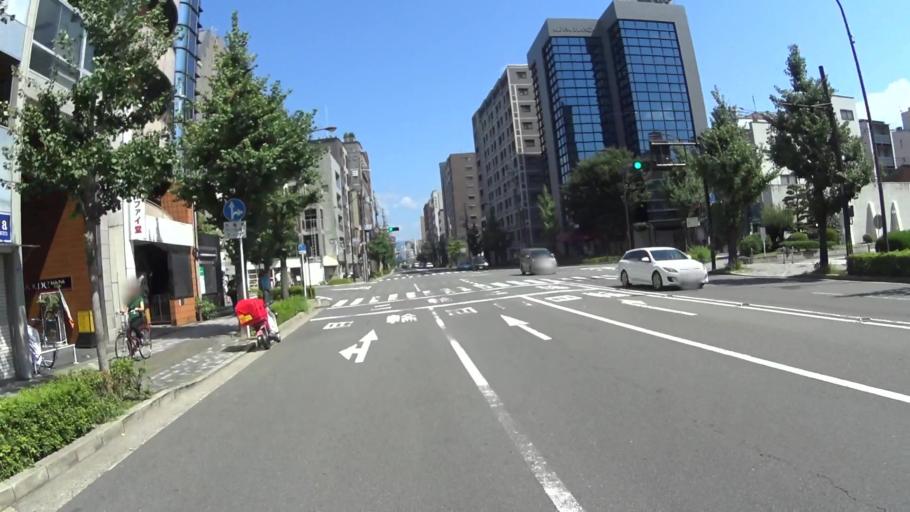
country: JP
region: Kyoto
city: Kyoto
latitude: 35.0124
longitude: 135.7692
